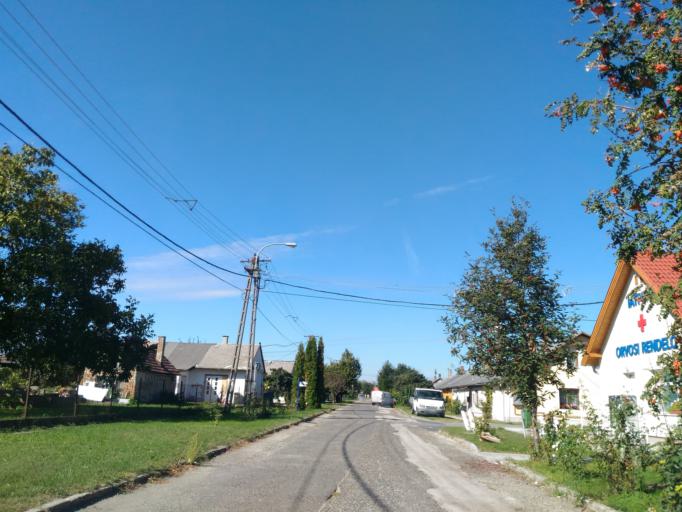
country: HU
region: Fejer
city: Ivancsa
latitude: 47.1837
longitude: 18.8234
